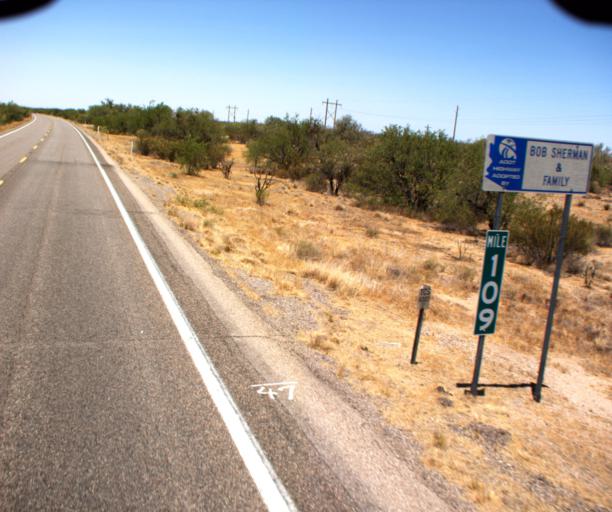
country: US
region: Arizona
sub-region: Pima County
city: Catalina
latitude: 32.7488
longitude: -111.1313
